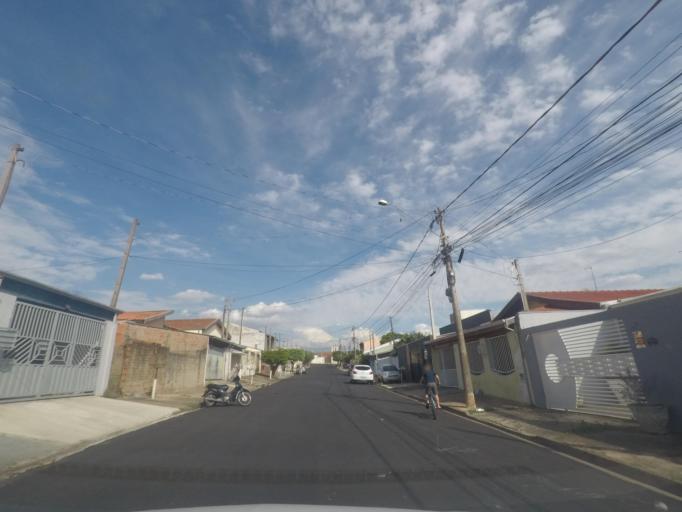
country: BR
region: Sao Paulo
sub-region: Sumare
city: Sumare
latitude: -22.8061
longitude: -47.2685
